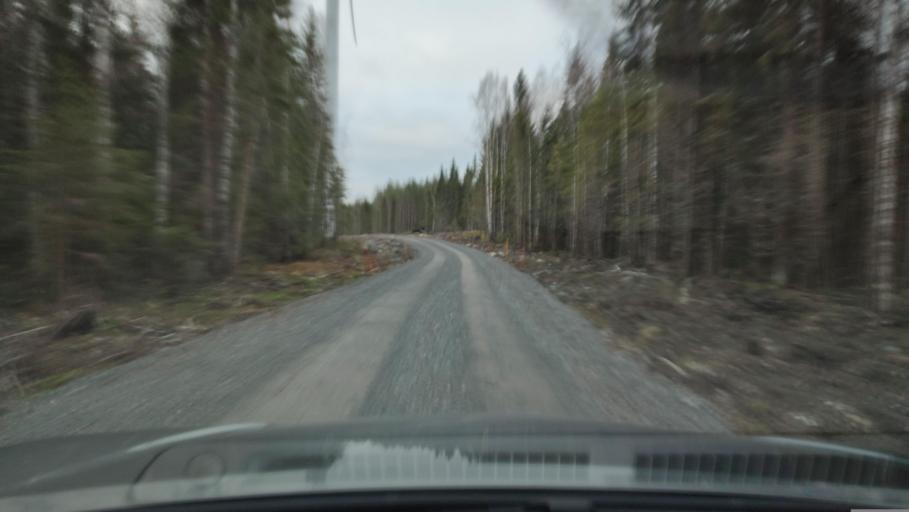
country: FI
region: Southern Ostrobothnia
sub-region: Suupohja
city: Karijoki
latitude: 62.1824
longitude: 21.5728
